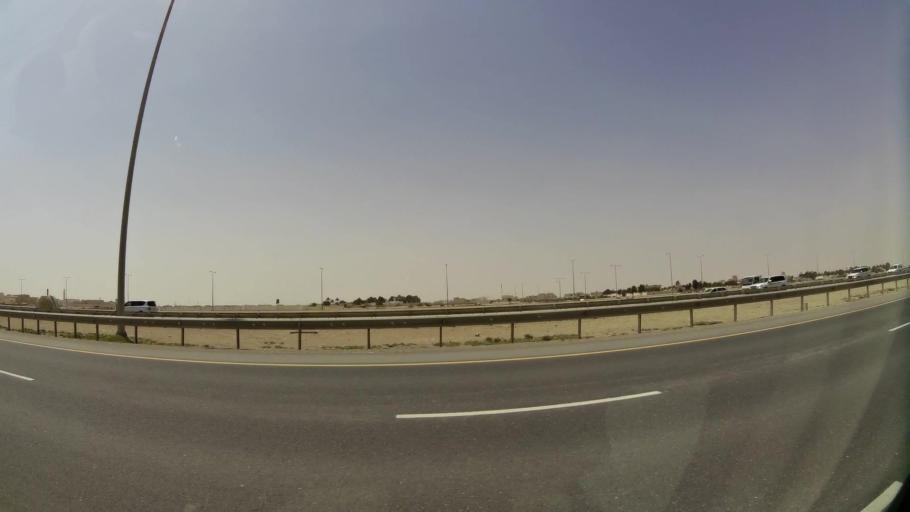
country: QA
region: Baladiyat Umm Salal
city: Umm Salal Muhammad
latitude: 25.4273
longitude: 51.4166
